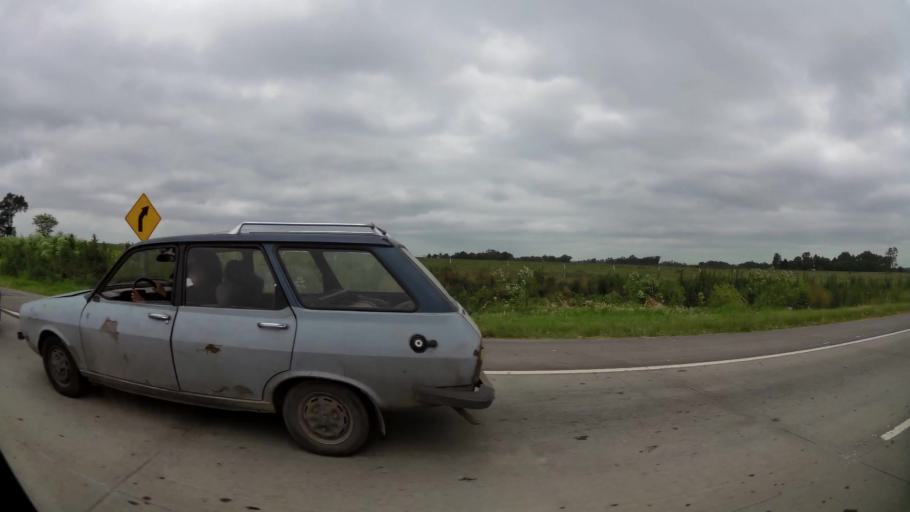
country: AR
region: Buenos Aires
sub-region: Partido de San Vicente
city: San Vicente
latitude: -35.0363
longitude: -58.3971
